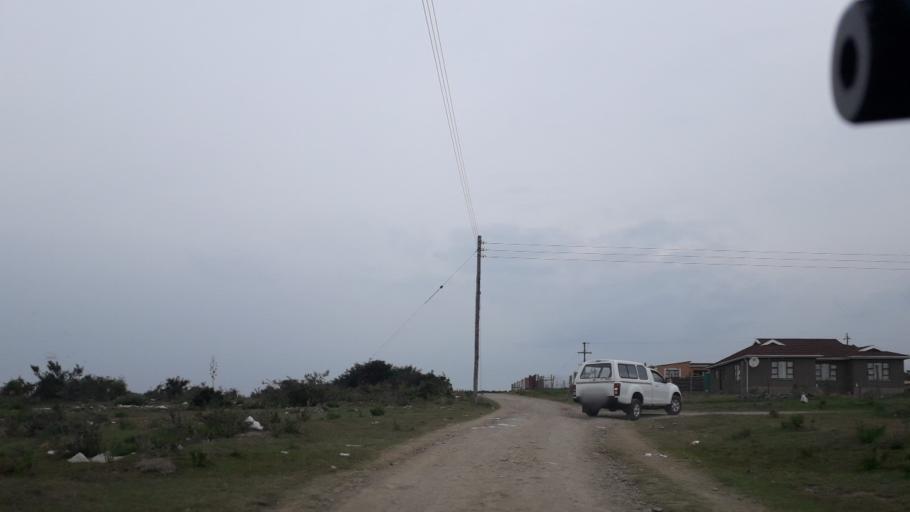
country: ZA
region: Eastern Cape
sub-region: Buffalo City Metropolitan Municipality
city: Bhisho
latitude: -32.8356
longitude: 27.3722
